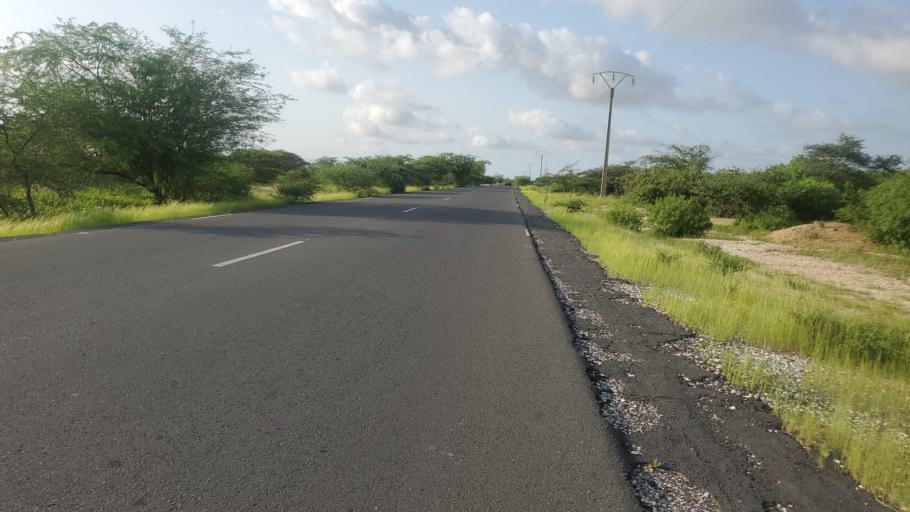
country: SN
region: Saint-Louis
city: Saint-Louis
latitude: 16.1137
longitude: -16.4133
